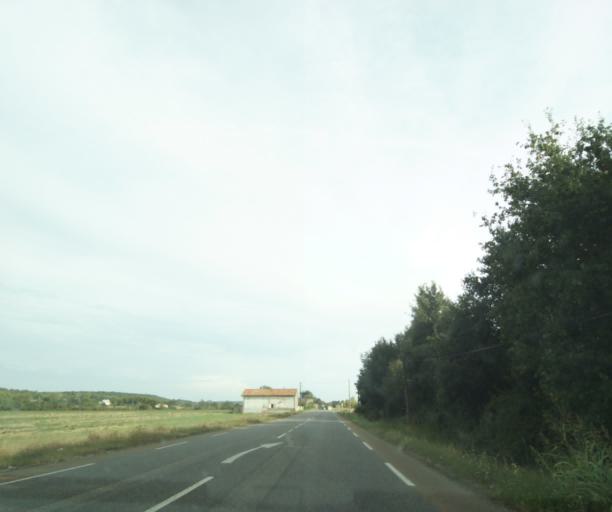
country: FR
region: Midi-Pyrenees
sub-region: Departement du Tarn-et-Garonne
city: Verdun-sur-Garonne
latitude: 43.8691
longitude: 1.2650
